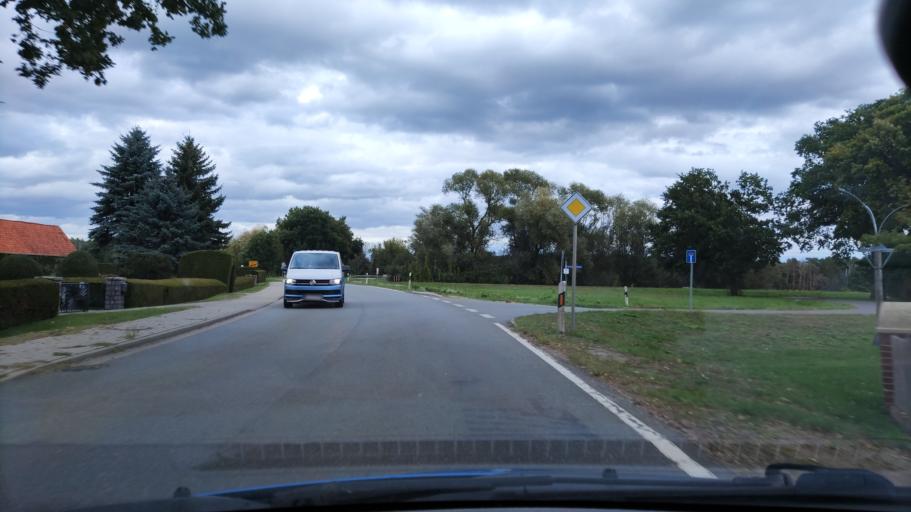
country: DE
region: Lower Saxony
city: Neu Darchau
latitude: 53.2994
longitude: 10.9675
